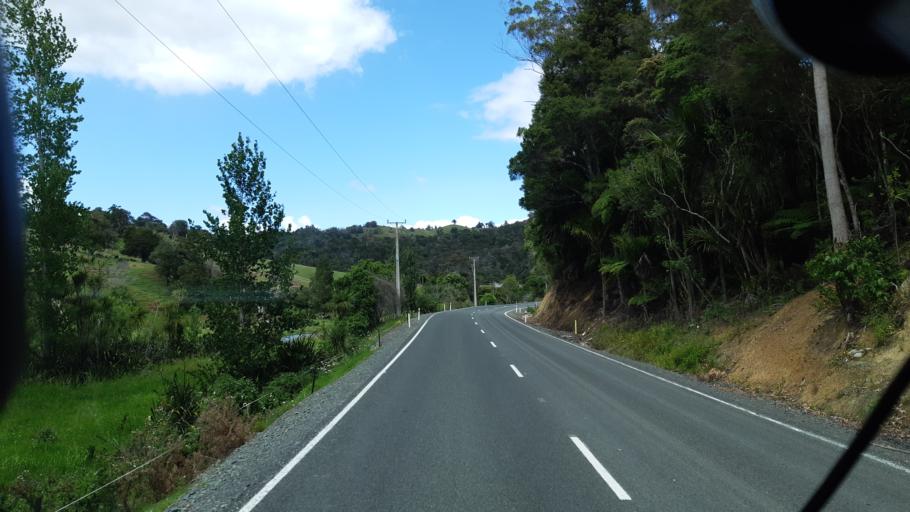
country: NZ
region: Northland
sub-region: Far North District
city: Taipa
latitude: -35.2410
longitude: 173.5400
